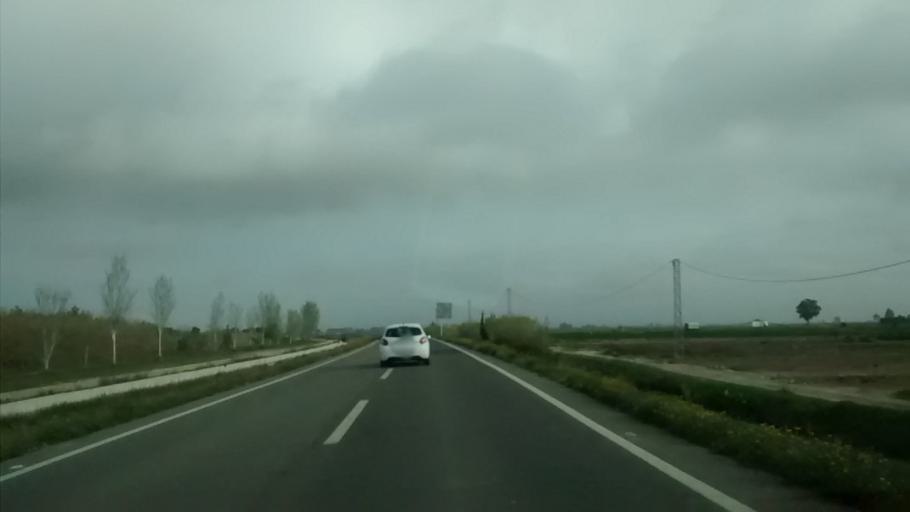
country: ES
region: Catalonia
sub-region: Provincia de Tarragona
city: Sant Carles de la Rapita
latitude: 40.6385
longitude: 0.6014
